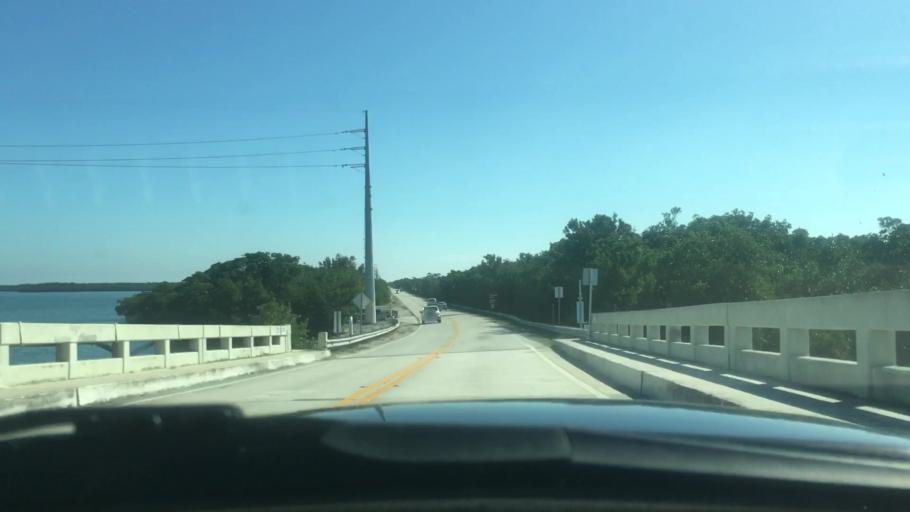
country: US
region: Florida
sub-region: Monroe County
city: North Key Largo
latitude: 25.2858
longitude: -80.3649
